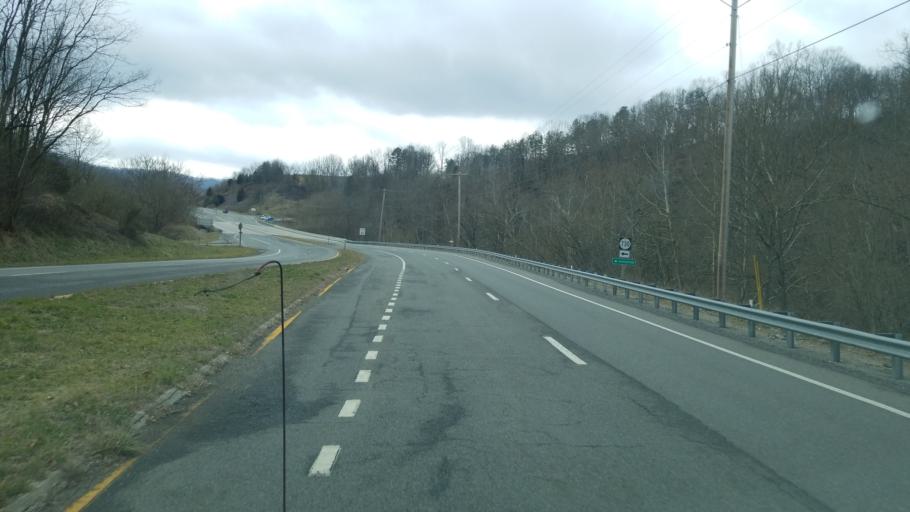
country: US
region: Virginia
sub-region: Giles County
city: Pearisburg
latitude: 37.2463
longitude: -80.7113
